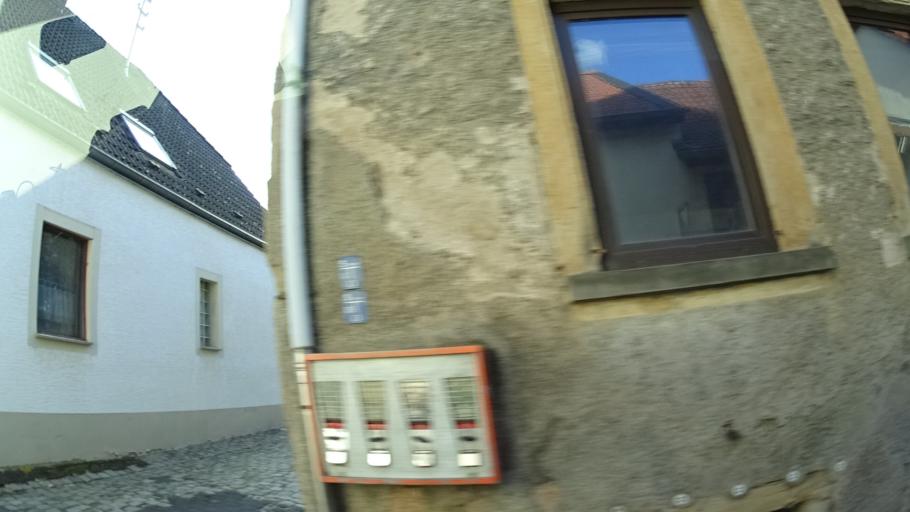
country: DE
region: Rheinland-Pfalz
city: Rehborn
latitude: 49.7344
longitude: 7.6868
